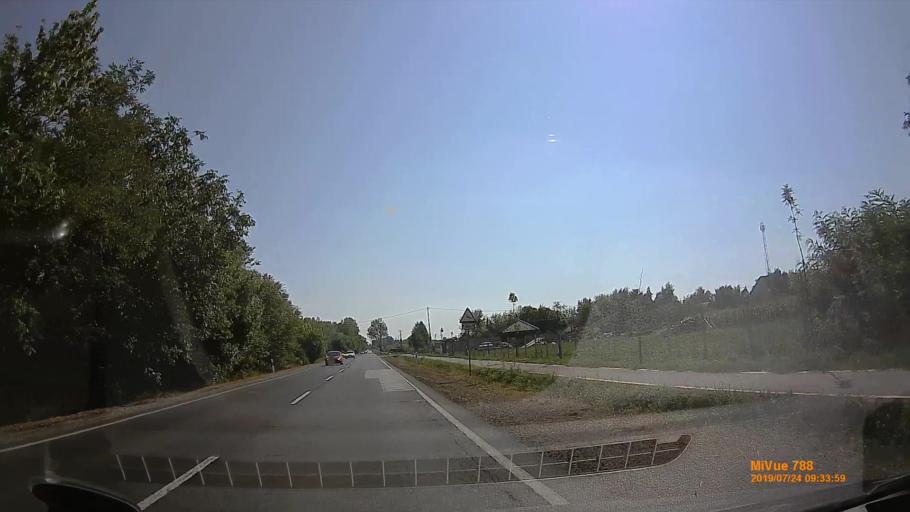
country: HU
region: Szabolcs-Szatmar-Bereg
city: Napkor
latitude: 47.9519
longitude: 21.8595
